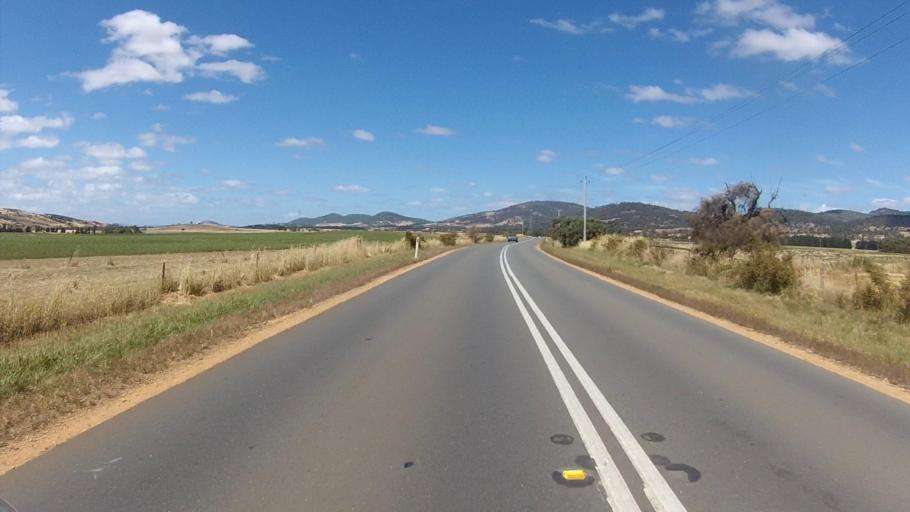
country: AU
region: Tasmania
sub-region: Clarence
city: Cambridge
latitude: -42.7574
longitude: 147.4154
